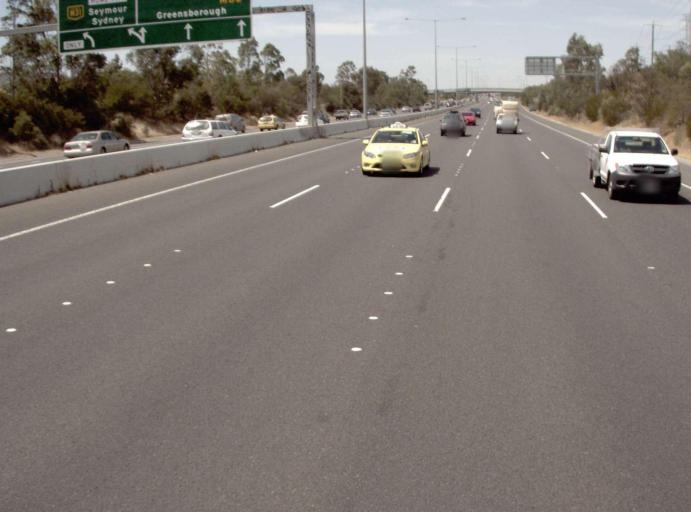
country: AU
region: Victoria
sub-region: Hume
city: Campbellfield
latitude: -37.6908
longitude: 144.9731
